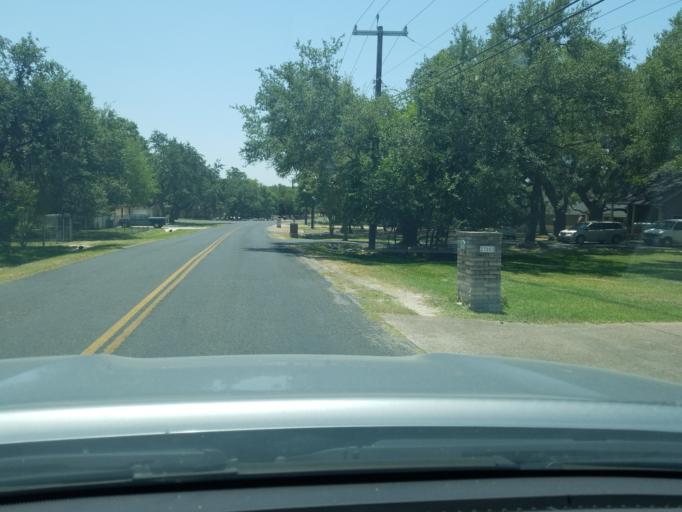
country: US
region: Texas
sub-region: Bexar County
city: Timberwood Park
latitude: 29.6999
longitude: -98.4892
